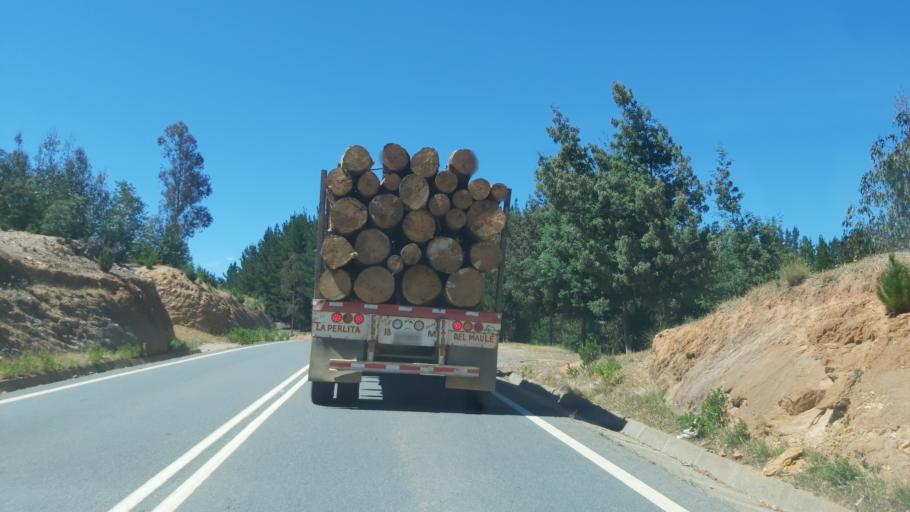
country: CL
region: Maule
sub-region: Provincia de Talca
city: Talca
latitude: -34.9408
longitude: -71.9793
